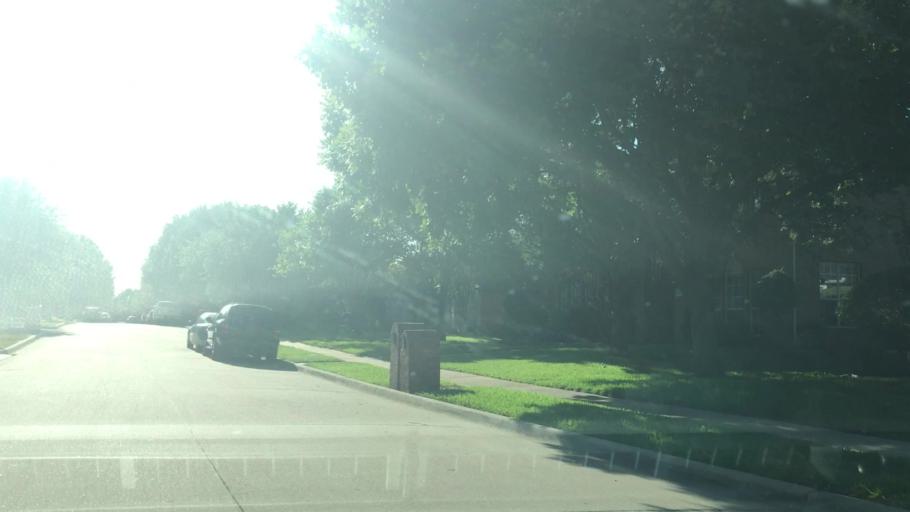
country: US
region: Texas
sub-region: Collin County
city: Frisco
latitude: 33.1221
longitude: -96.7783
